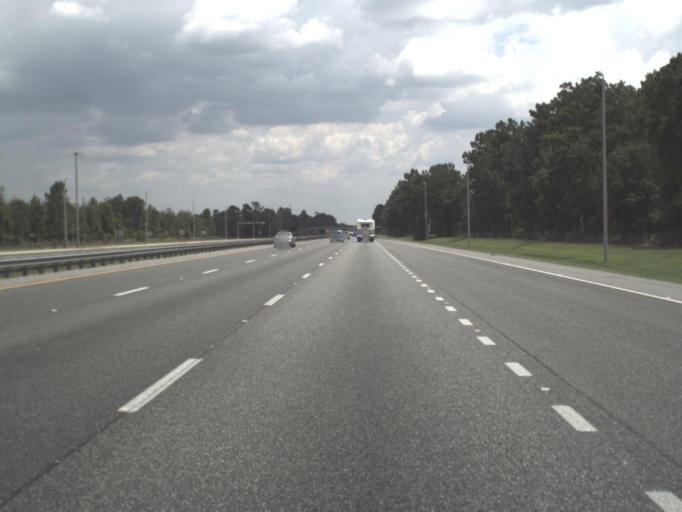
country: US
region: Florida
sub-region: Hamilton County
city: Jasper
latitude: 30.4141
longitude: -82.8962
